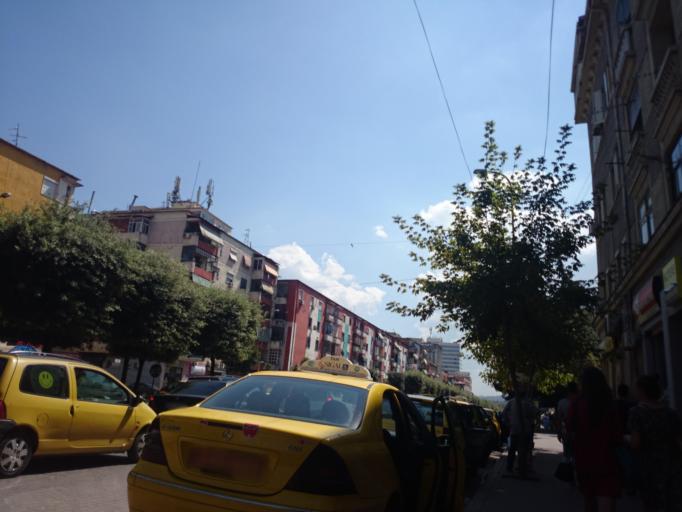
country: AL
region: Tirane
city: Tirana
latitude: 41.3336
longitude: 19.8168
